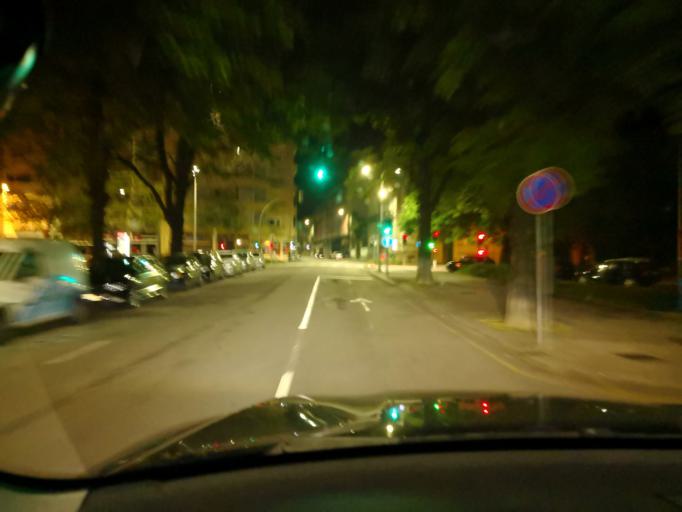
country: PT
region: Porto
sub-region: Porto
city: Porto
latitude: 41.1460
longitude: -8.5962
